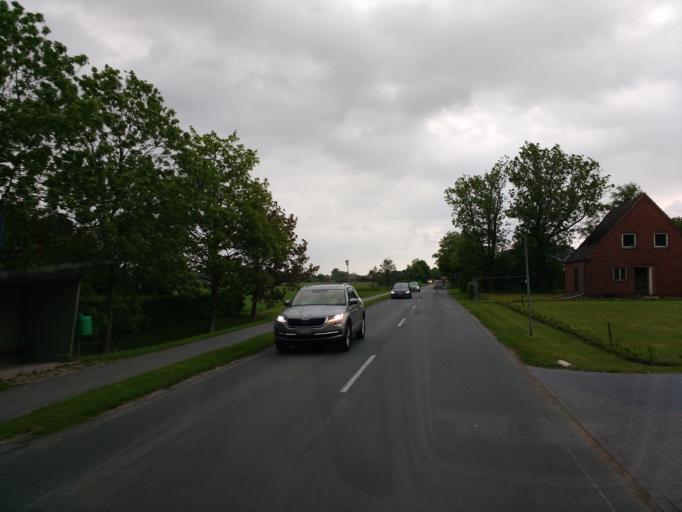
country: DE
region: Lower Saxony
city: Sillenstede
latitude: 53.6370
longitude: 8.0099
